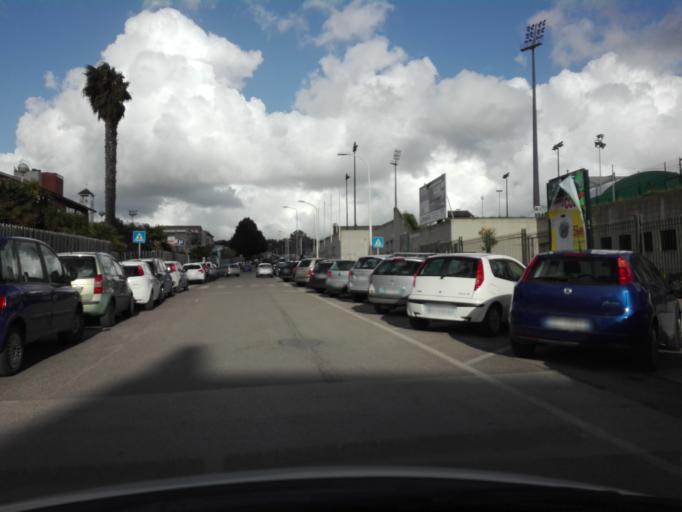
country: IT
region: Sardinia
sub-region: Provincia di Sassari
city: Sassari
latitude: 40.7190
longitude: 8.5781
